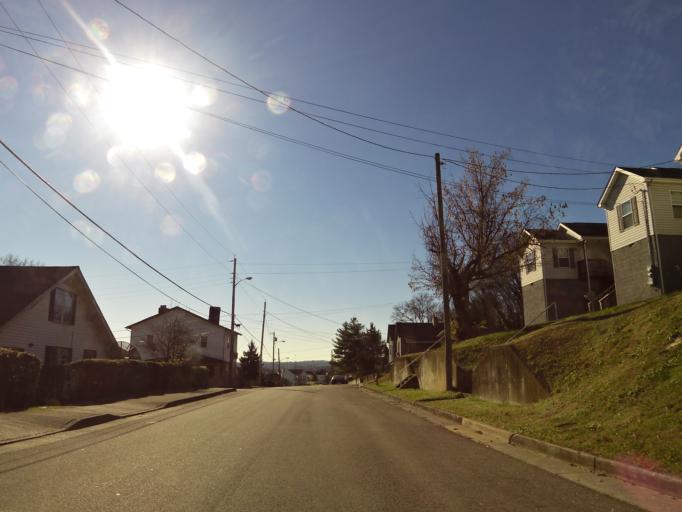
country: US
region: Tennessee
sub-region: Knox County
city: Knoxville
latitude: 35.9705
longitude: -83.9385
